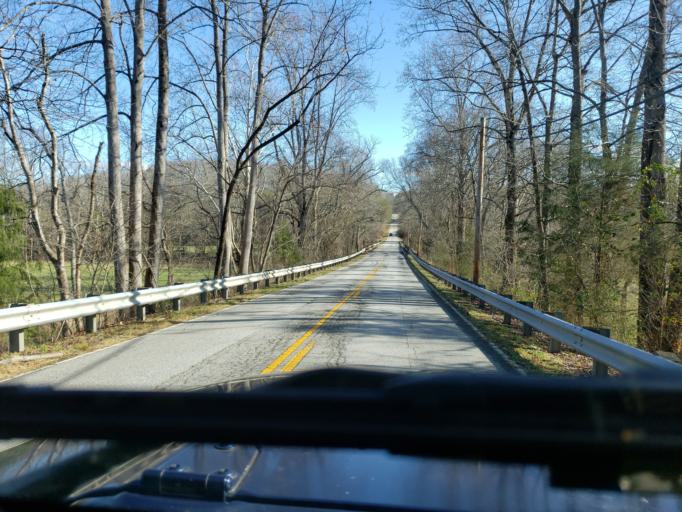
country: US
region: North Carolina
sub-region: Cleveland County
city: White Plains
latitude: 35.1573
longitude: -81.4020
